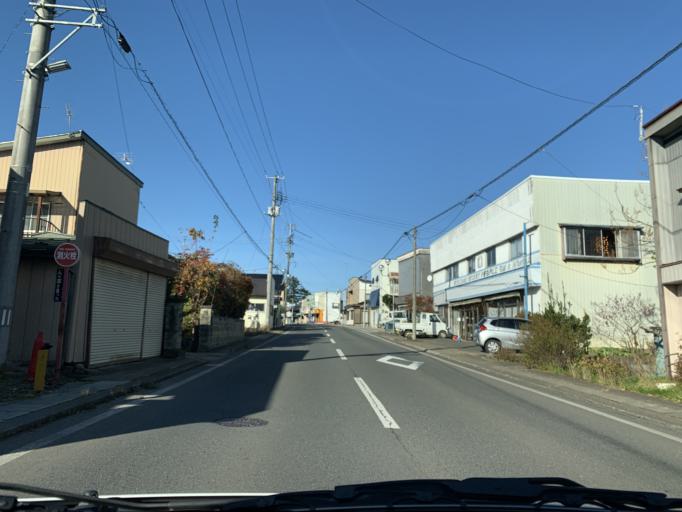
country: JP
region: Iwate
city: Mizusawa
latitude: 39.1941
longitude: 141.1190
